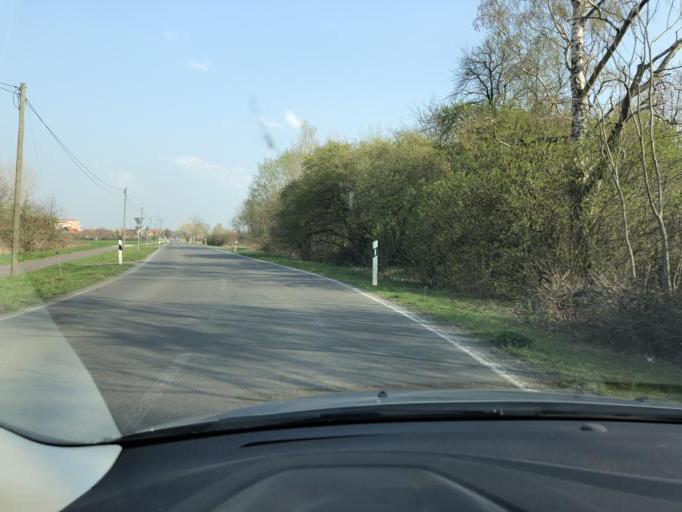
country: DE
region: Saxony
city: Rackwitz
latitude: 51.4333
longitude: 12.3574
